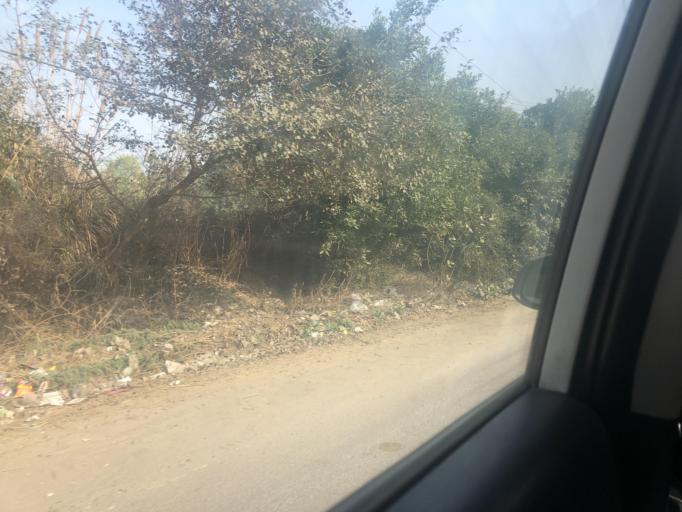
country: IN
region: Haryana
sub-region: Jhajjar
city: Bahadurgarh
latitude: 28.6871
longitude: 76.8879
